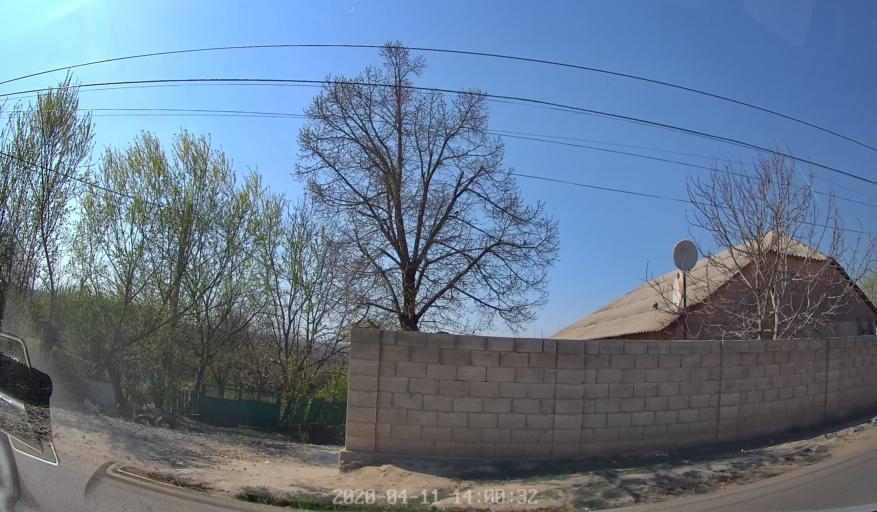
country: MD
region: Chisinau
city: Vadul lui Voda
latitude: 47.0847
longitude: 29.1334
